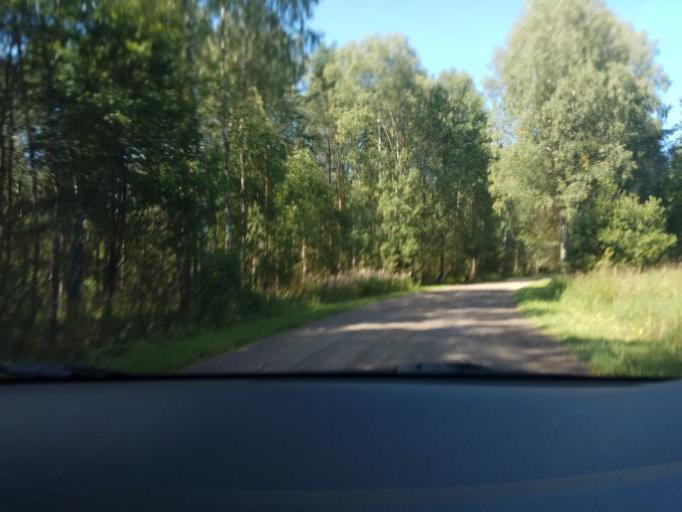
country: RU
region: Vladimir
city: Dobryatino
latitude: 55.7385
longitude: 41.4312
